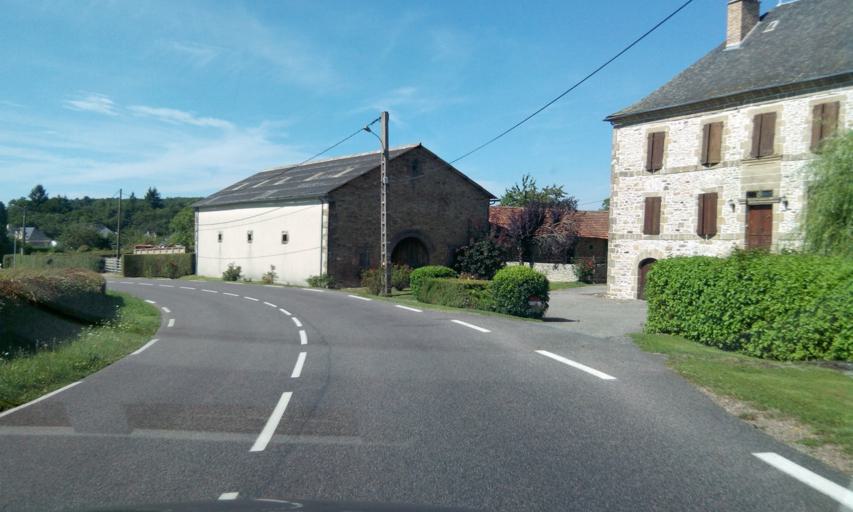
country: FR
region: Limousin
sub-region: Departement de la Correze
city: Beynat
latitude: 45.1332
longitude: 1.7839
